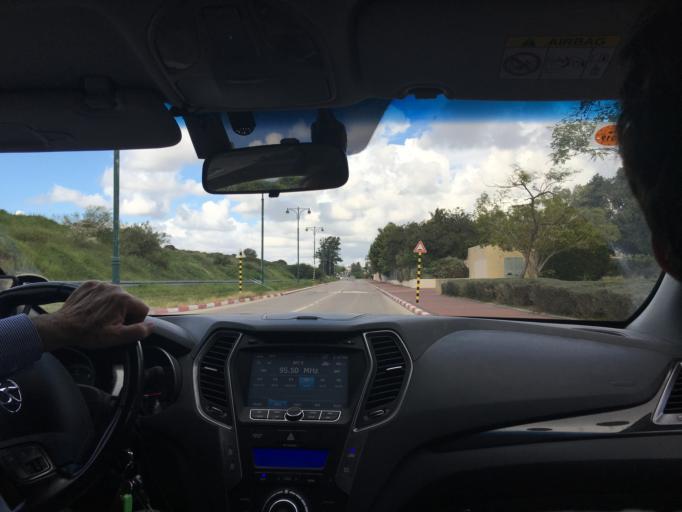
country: IL
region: Central District
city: Ness Ziona
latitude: 31.9331
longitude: 34.7866
